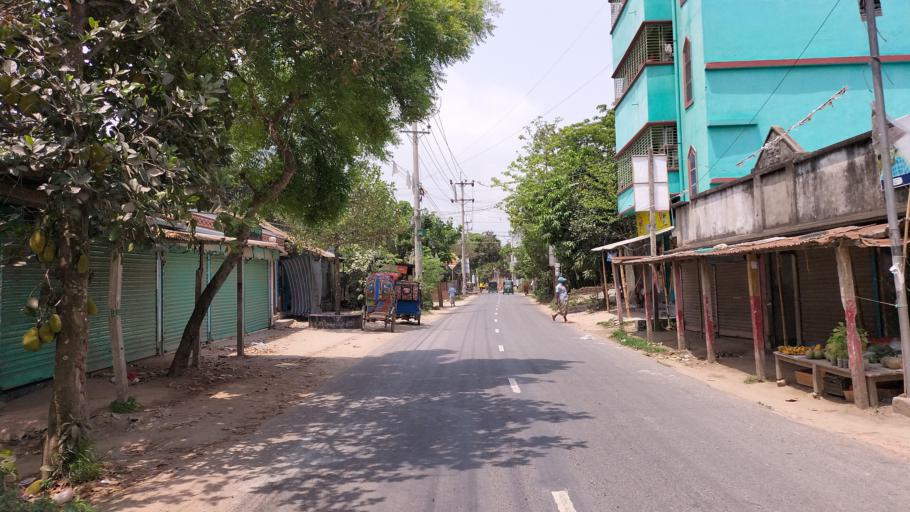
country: BD
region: Dhaka
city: Azimpur
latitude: 23.7291
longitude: 90.2899
